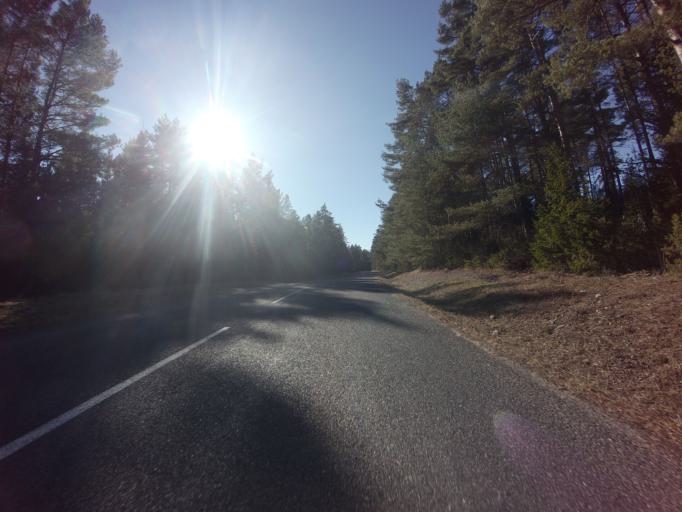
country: EE
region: Saare
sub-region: Kuressaare linn
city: Kuressaare
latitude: 58.5955
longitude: 22.5879
